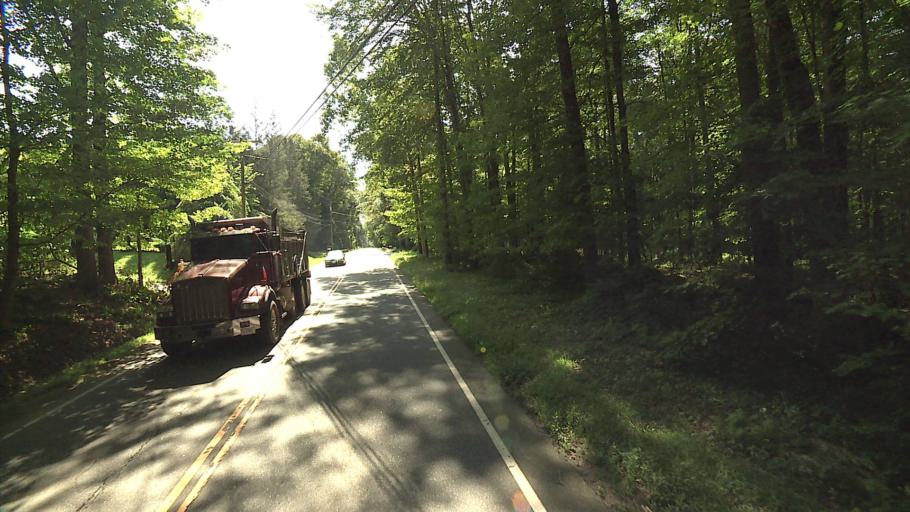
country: US
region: Connecticut
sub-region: New London County
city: Colchester
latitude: 41.6286
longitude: -72.2913
